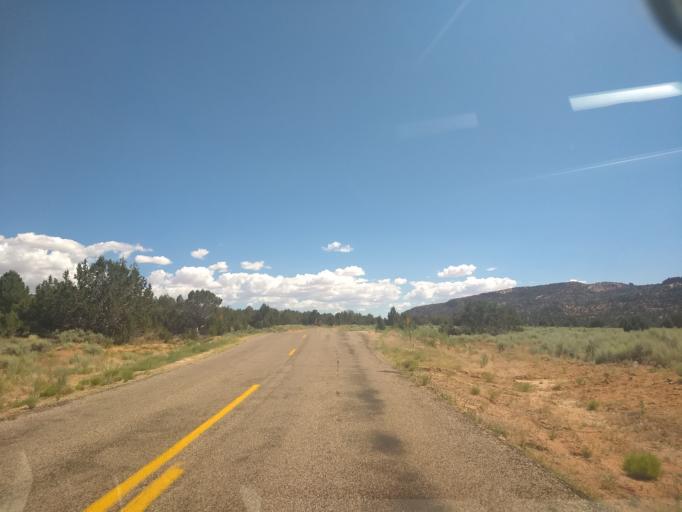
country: US
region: Utah
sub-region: Washington County
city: Hildale
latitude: 36.9977
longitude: -112.8630
